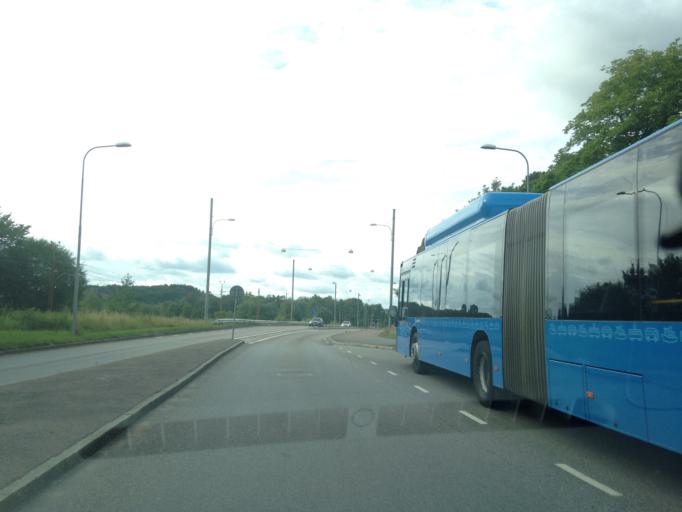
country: SE
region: Vaestra Goetaland
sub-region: Goteborg
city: Goeteborg
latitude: 57.7474
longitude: 11.9510
